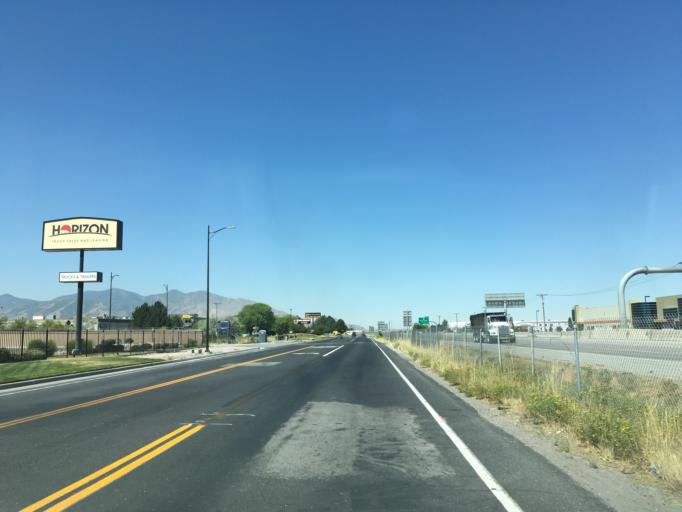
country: US
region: Utah
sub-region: Salt Lake County
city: West Valley City
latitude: 40.7256
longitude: -112.0048
